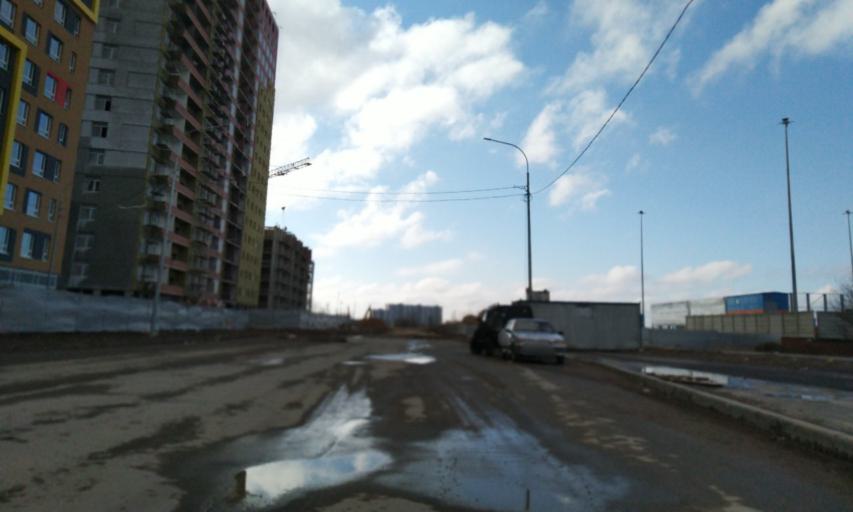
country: RU
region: Leningrad
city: Murino
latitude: 60.0688
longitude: 30.4291
